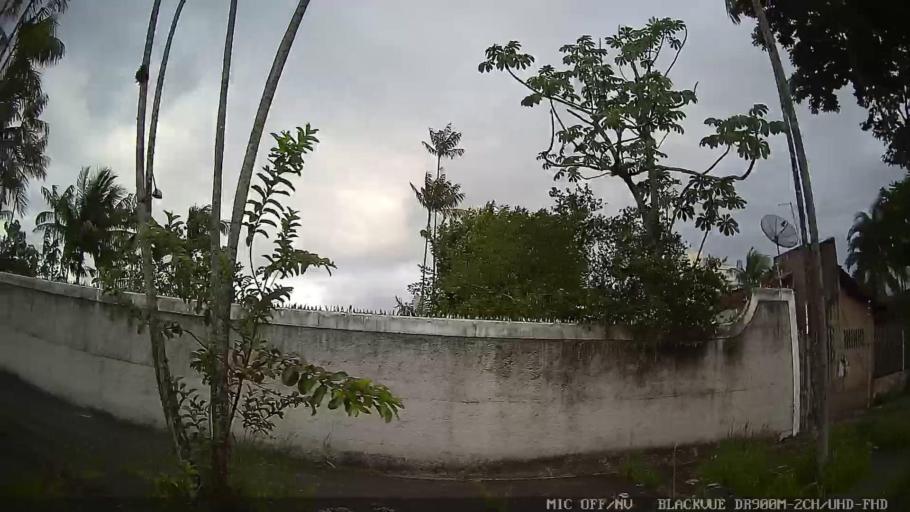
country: BR
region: Sao Paulo
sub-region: Caraguatatuba
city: Caraguatatuba
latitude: -23.6349
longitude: -45.4238
